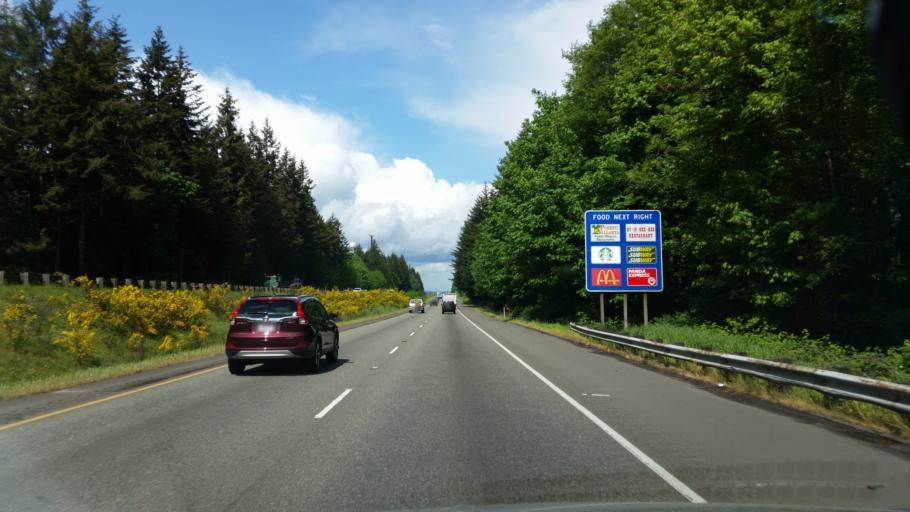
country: US
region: Washington
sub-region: Pierce County
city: Gig Harbor
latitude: 47.3419
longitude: -122.6069
